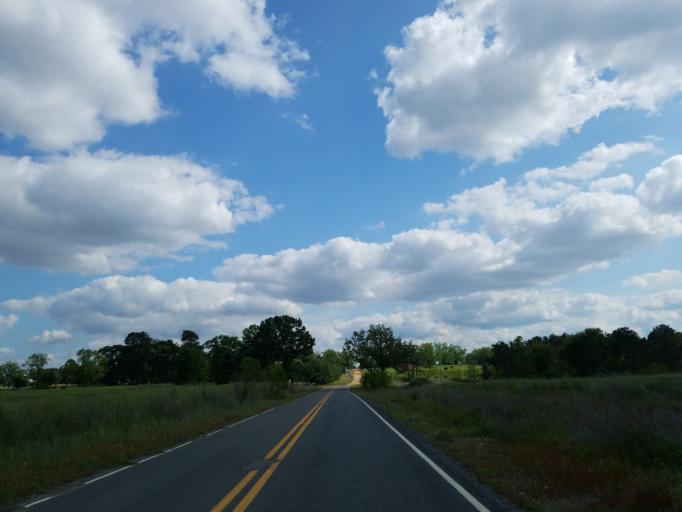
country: US
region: Georgia
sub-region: Dooly County
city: Unadilla
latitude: 32.2577
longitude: -83.7873
